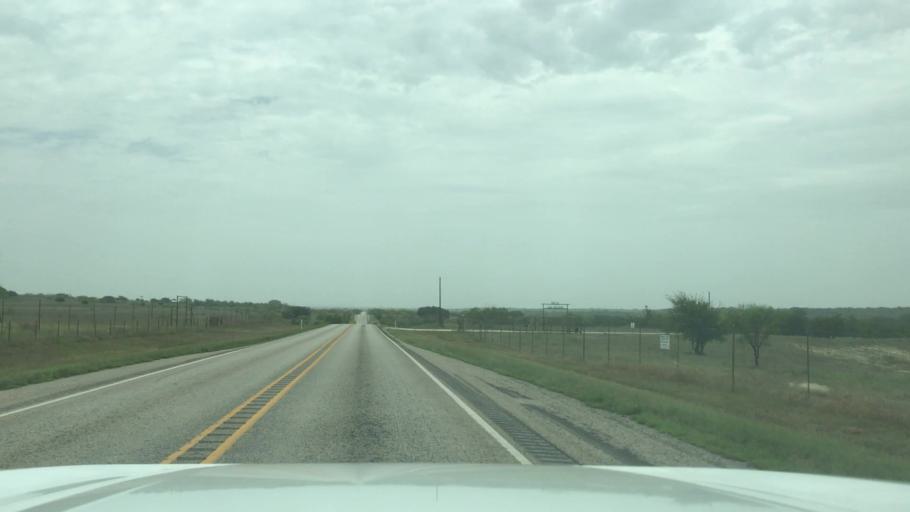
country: US
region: Texas
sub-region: Hamilton County
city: Hico
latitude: 32.0534
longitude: -98.1727
